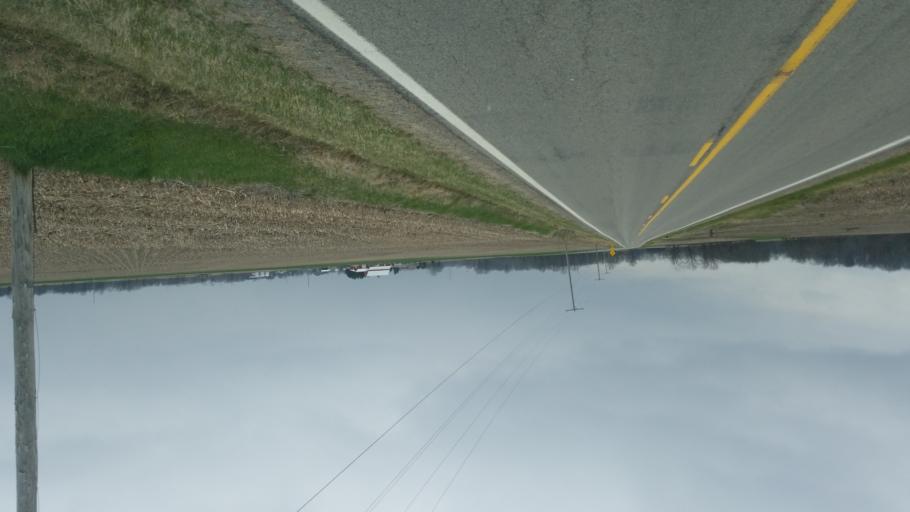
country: US
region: Ohio
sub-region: Union County
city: Richwood
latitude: 40.4004
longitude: -83.3877
